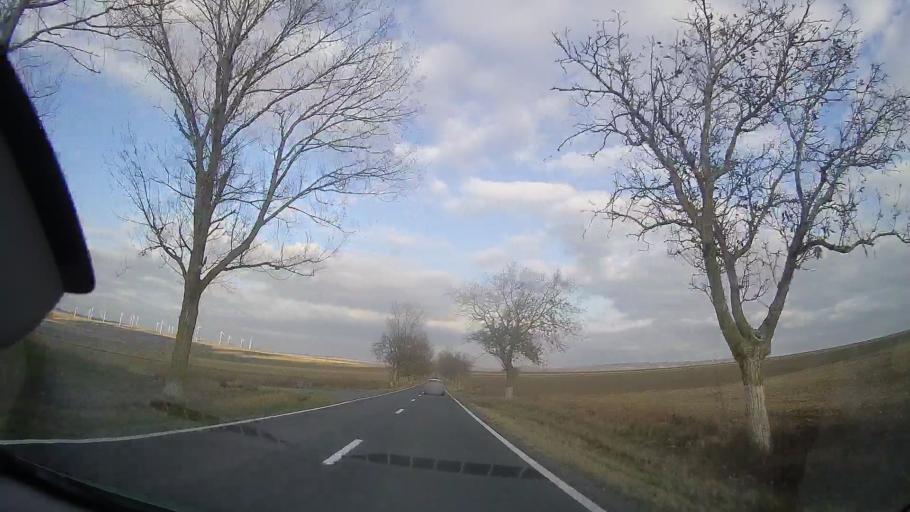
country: RO
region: Tulcea
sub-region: Comuna Topolog
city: Topolog
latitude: 44.8559
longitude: 28.3355
